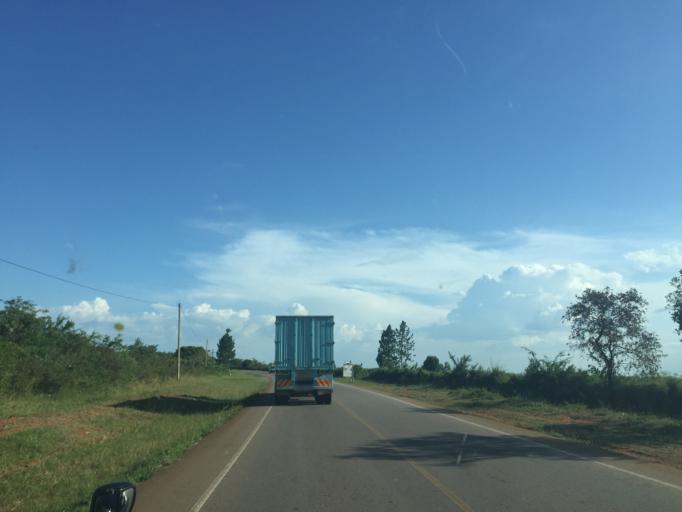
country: UG
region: Central Region
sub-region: Nakasongola District
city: Nakasongola
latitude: 1.2983
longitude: 32.4225
